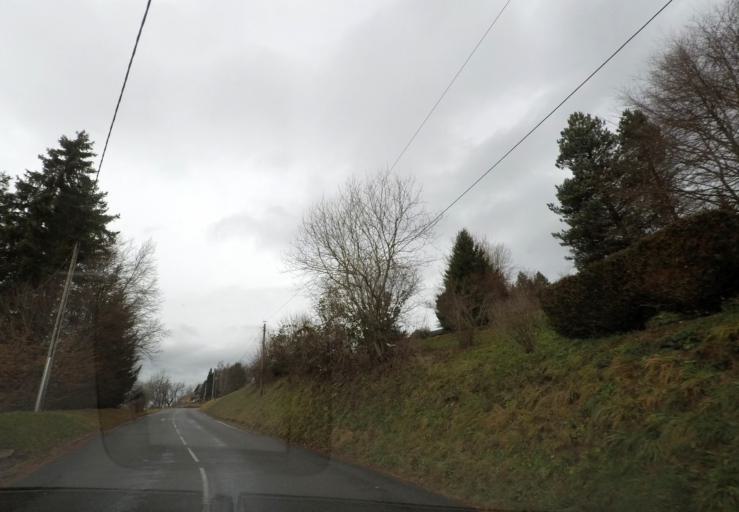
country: FR
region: Rhone-Alpes
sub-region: Departement de la Haute-Savoie
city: Chatillon-sur-Cluses
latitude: 46.0769
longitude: 6.6130
